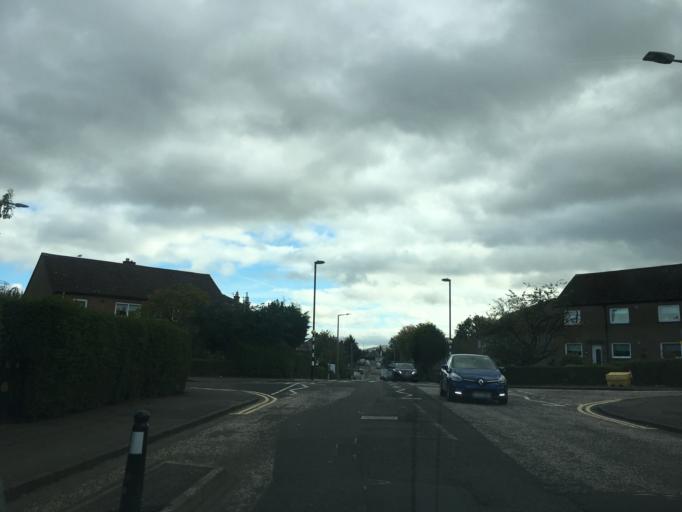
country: GB
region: Scotland
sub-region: Edinburgh
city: Edinburgh
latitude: 55.9637
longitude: -3.2488
